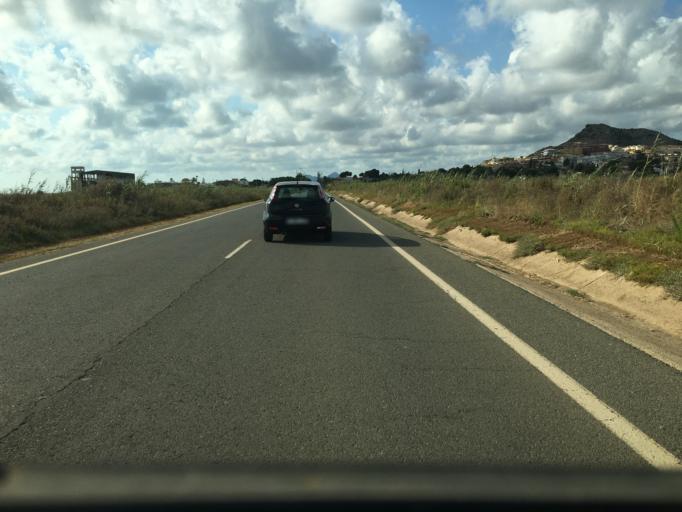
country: ES
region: Murcia
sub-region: Murcia
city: Los Alcazares
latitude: 37.6988
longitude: -0.8449
